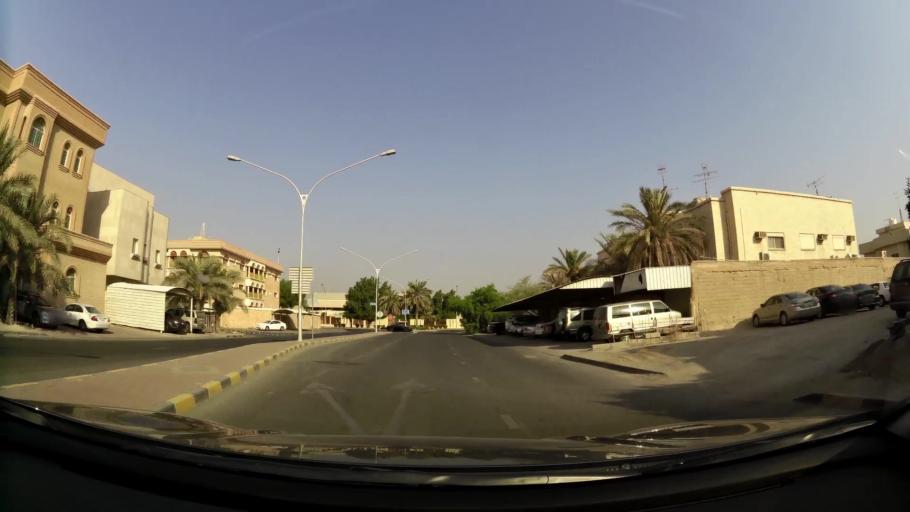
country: KW
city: Bayan
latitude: 29.3182
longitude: 48.0435
